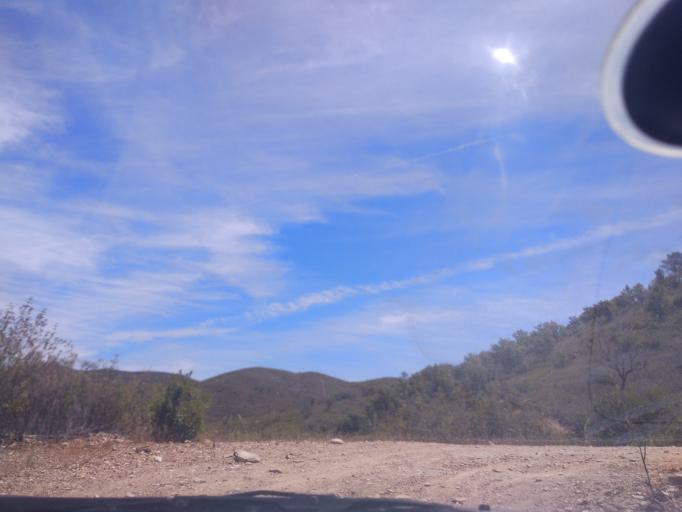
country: PT
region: Faro
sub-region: Sao Bras de Alportel
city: Sao Bras de Alportel
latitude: 37.2134
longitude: -7.8185
